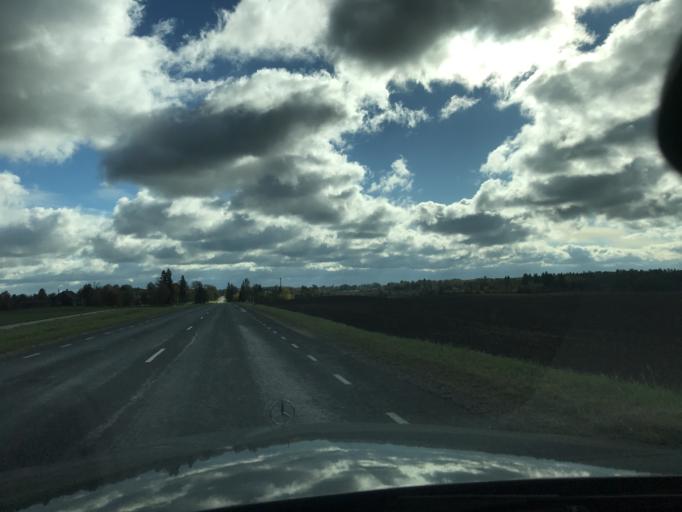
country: EE
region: Vorumaa
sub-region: Antsla vald
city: Vana-Antsla
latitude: 57.9514
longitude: 26.2853
